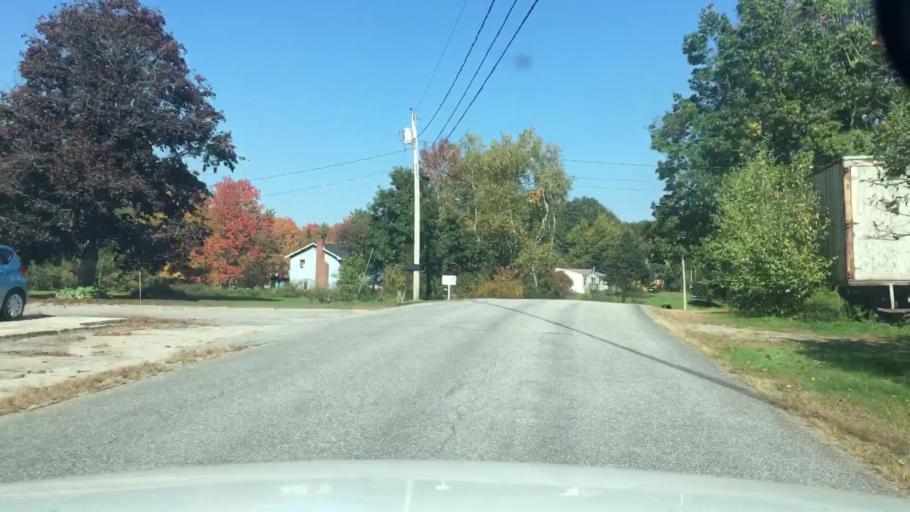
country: US
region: Maine
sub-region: Androscoggin County
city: Lisbon Falls
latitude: 44.0326
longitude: -69.9862
